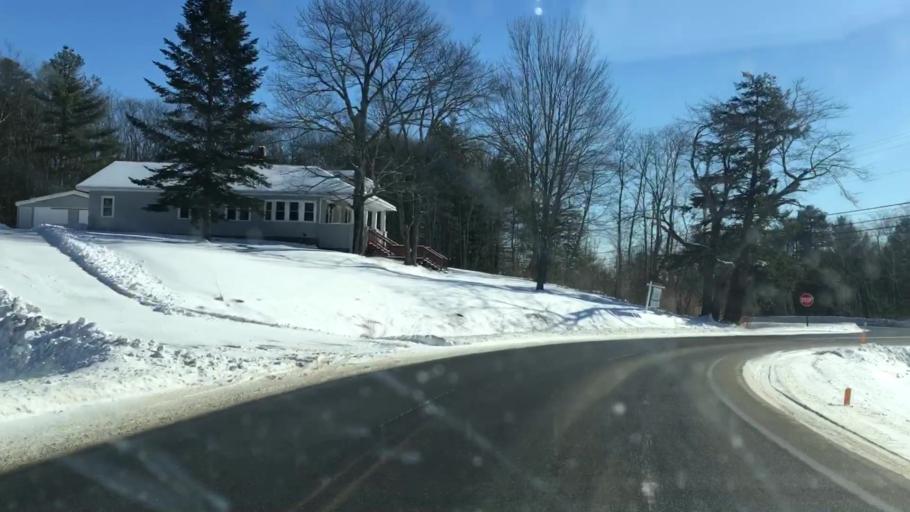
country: US
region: Maine
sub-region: Sagadahoc County
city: Topsham
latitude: 43.9109
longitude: -70.0151
